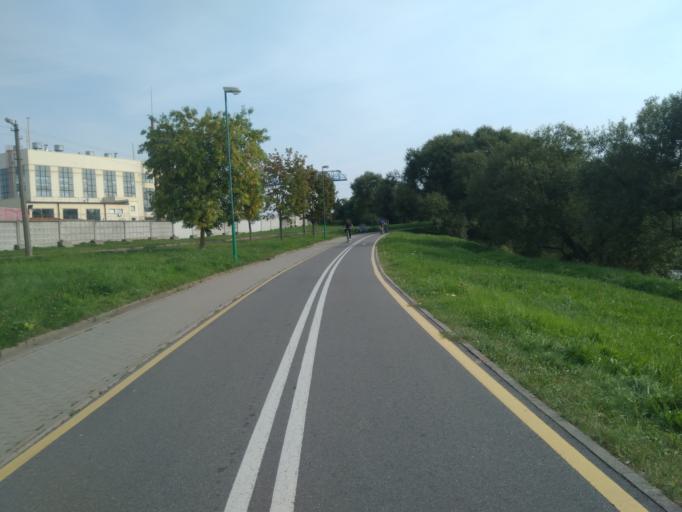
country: BY
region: Minsk
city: Minsk
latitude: 53.8819
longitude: 27.5749
